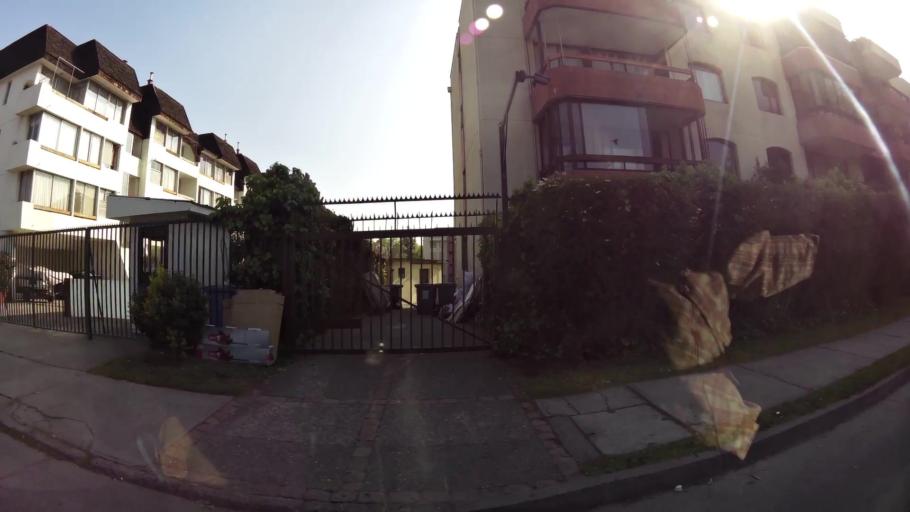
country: CL
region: Santiago Metropolitan
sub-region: Provincia de Santiago
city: Villa Presidente Frei, Nunoa, Santiago, Chile
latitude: -33.3828
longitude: -70.5500
